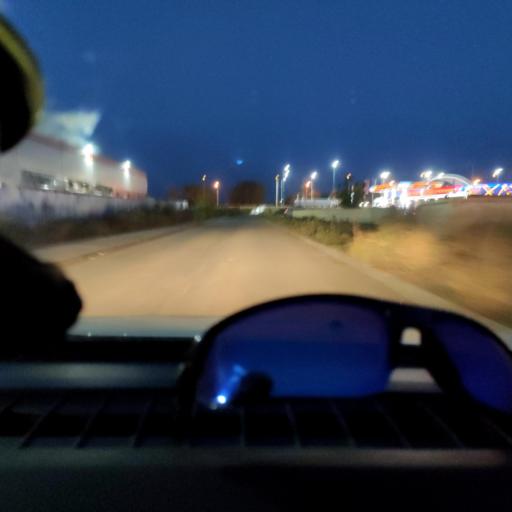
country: RU
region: Samara
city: Samara
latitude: 53.1141
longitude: 50.1628
